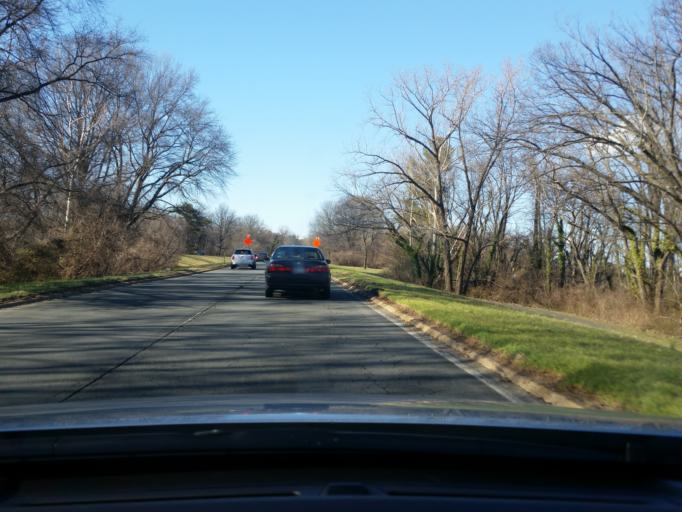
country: US
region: Virginia
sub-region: City of Alexandria
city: Alexandria
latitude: 38.8324
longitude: -77.0442
